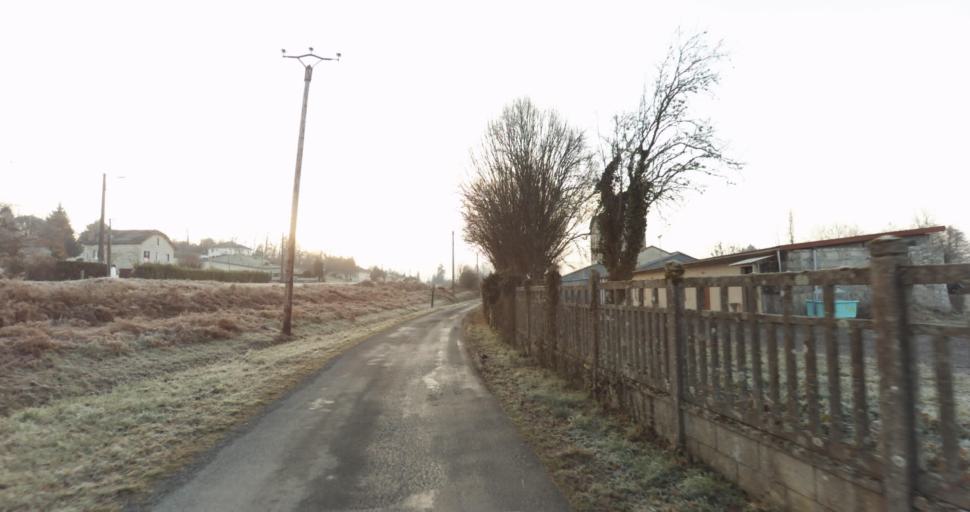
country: FR
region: Limousin
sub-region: Departement de la Haute-Vienne
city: Aixe-sur-Vienne
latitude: 45.8047
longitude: 1.1233
